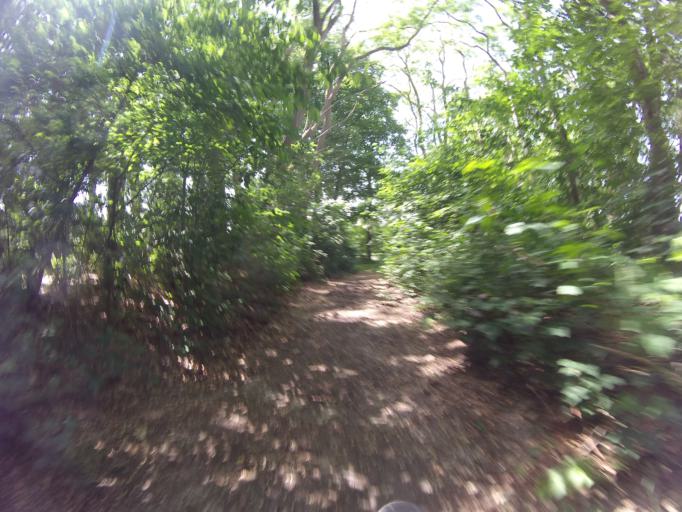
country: NL
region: Gelderland
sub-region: Gemeente Ede
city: Lunteren
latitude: 52.1033
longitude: 5.6420
